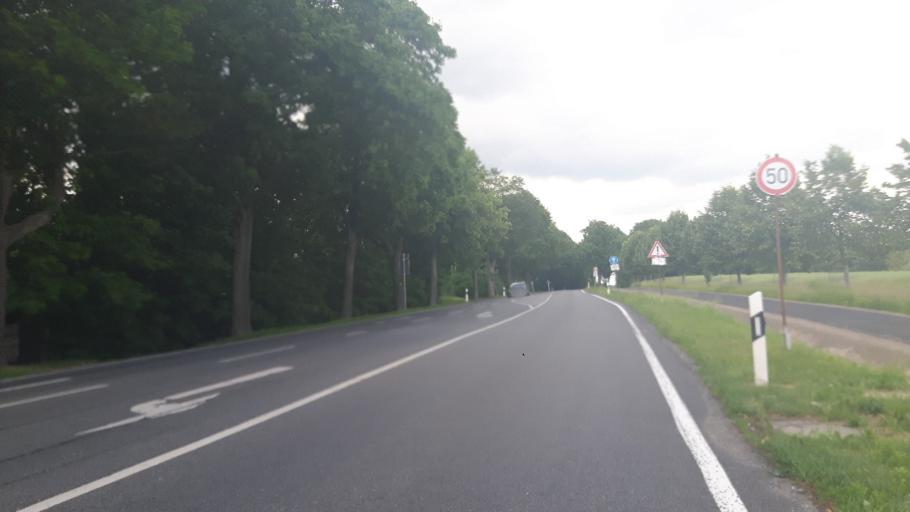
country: DE
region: Brandenburg
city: Bernau bei Berlin
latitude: 52.6452
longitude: 13.5651
